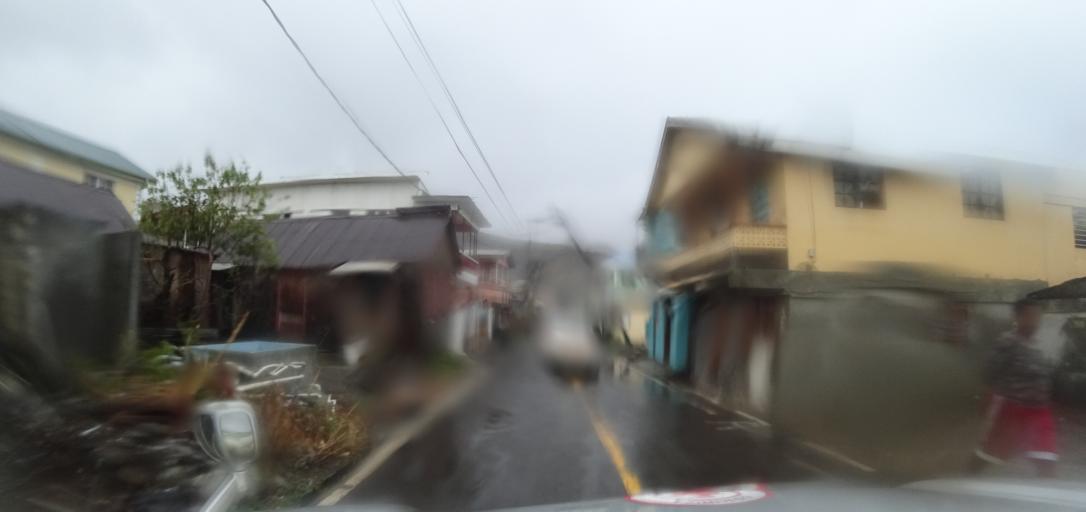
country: DM
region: Saint Paul
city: Mahaut
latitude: 15.3631
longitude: -61.3987
